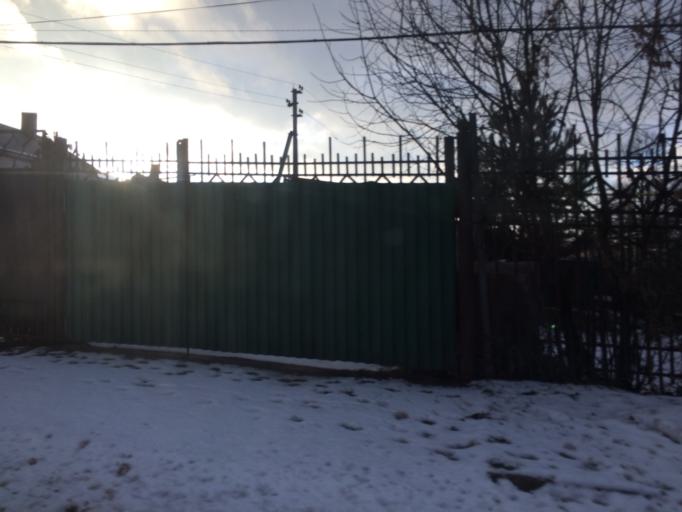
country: RU
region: Tula
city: Cherepet'
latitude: 54.1144
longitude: 36.3260
